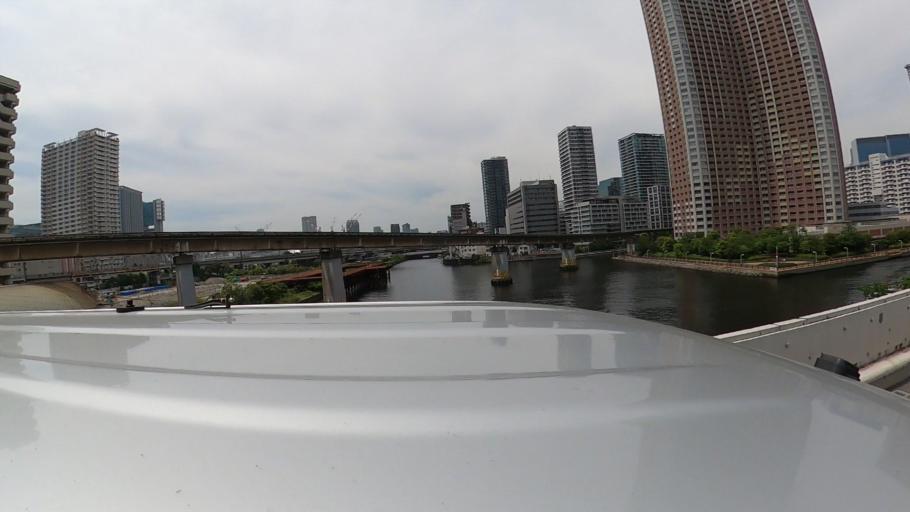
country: JP
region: Tokyo
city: Tokyo
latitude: 35.6355
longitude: 139.7514
